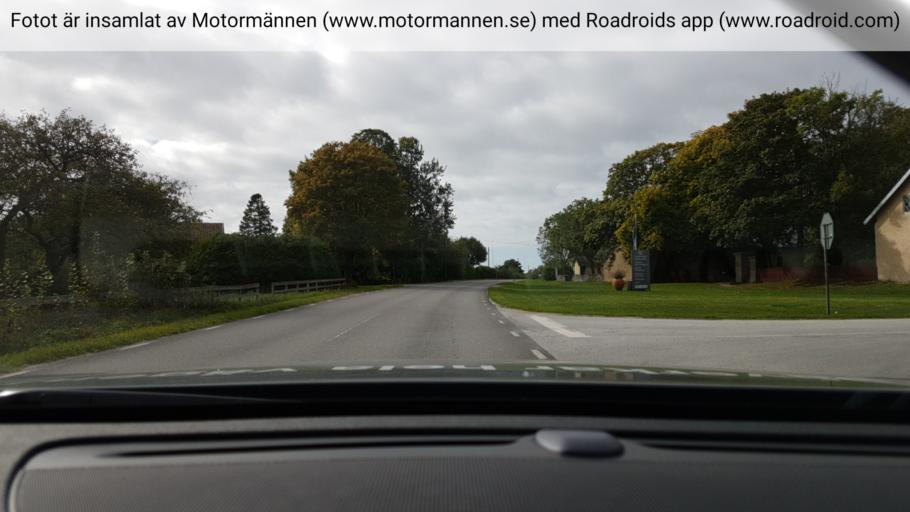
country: SE
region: Gotland
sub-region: Gotland
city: Hemse
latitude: 56.9695
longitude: 18.2325
